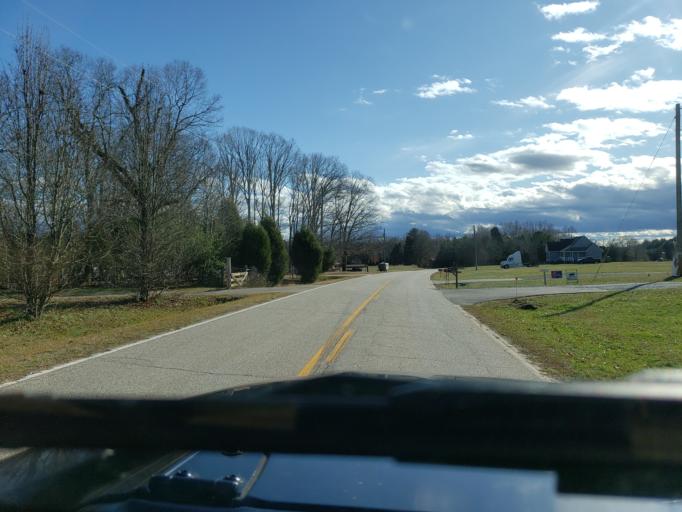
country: US
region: North Carolina
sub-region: Cleveland County
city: White Plains
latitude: 35.1638
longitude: -81.4057
